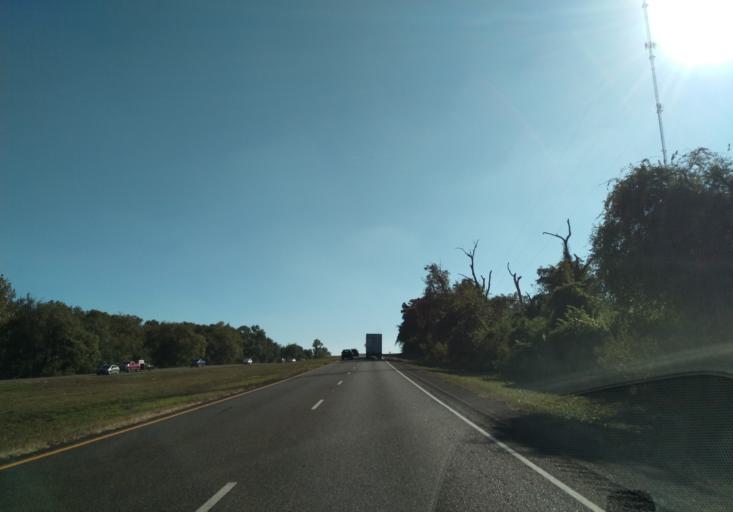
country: US
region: Texas
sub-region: Grimes County
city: Navasota
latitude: 30.2513
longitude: -96.0457
